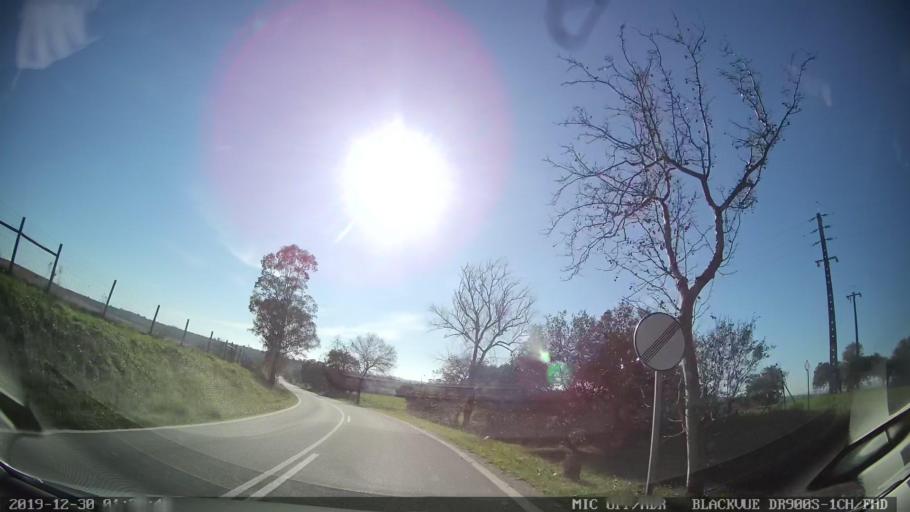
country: PT
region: Castelo Branco
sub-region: Idanha-A-Nova
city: Idanha-a-Nova
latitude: 39.8898
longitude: -7.2068
